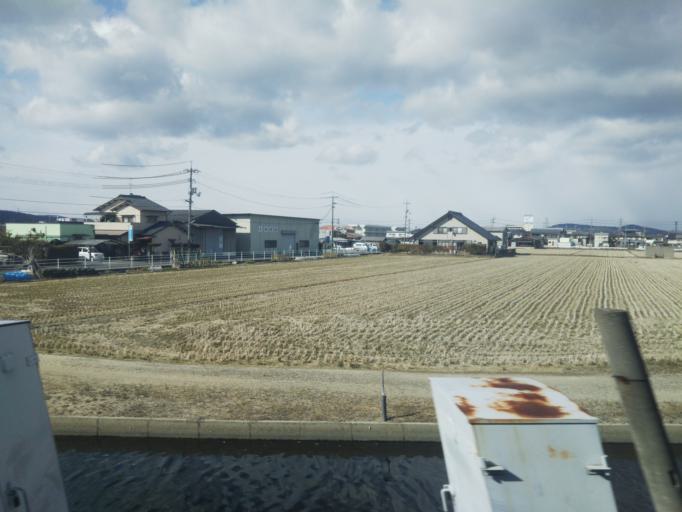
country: JP
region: Okayama
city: Okayama-shi
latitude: 34.6101
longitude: 133.8755
